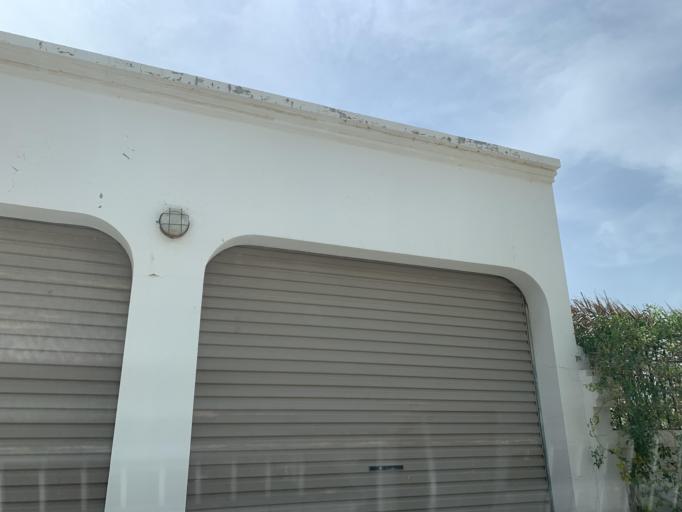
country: BH
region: Northern
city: Ar Rifa'
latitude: 26.1449
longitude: 50.5624
